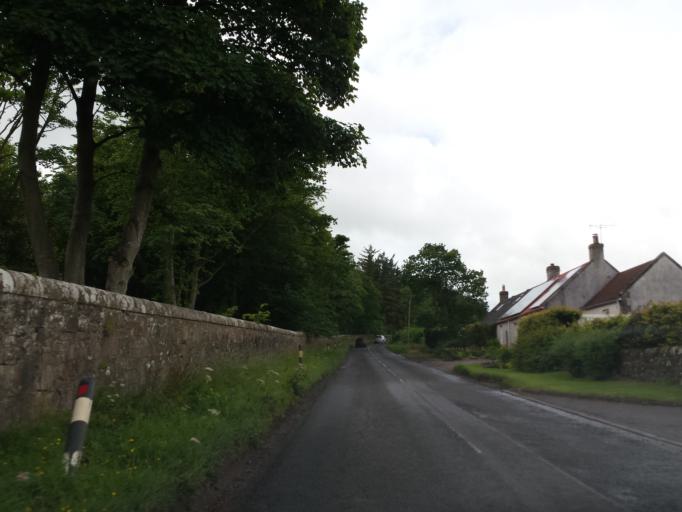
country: GB
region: Scotland
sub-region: Fife
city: Strathkinness
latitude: 56.3233
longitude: -2.8481
